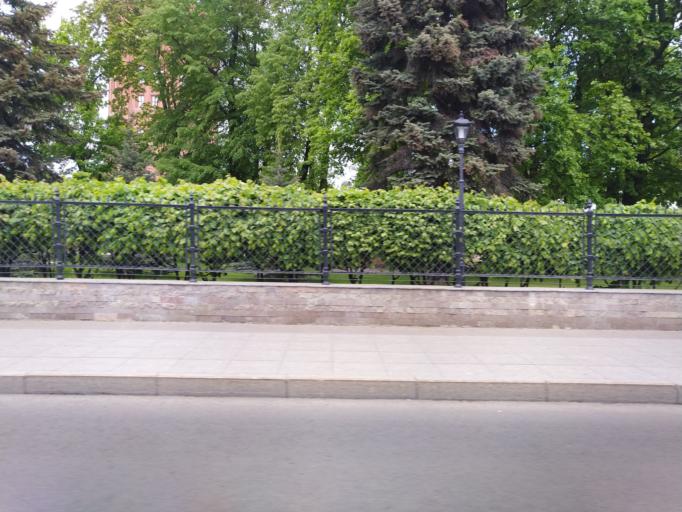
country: RU
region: Leningrad
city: Finlyandskiy
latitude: 59.9487
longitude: 30.3767
